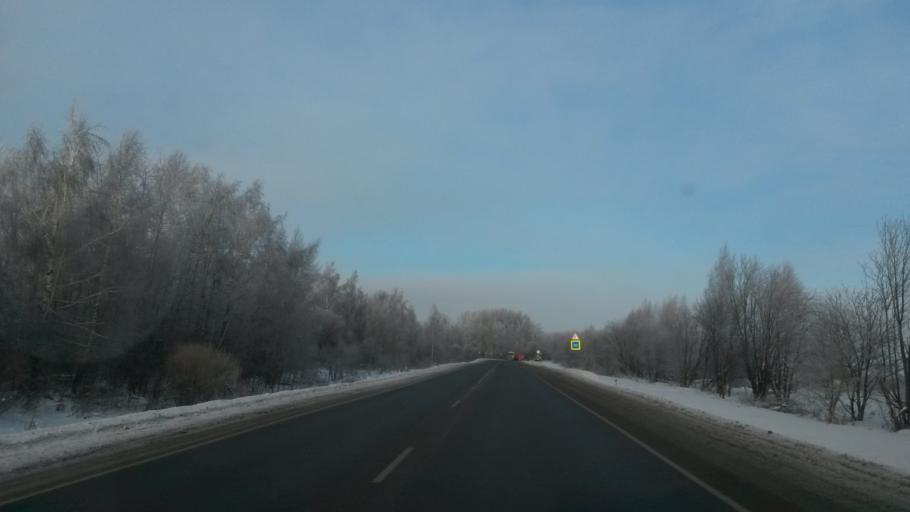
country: RU
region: Vladimir
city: Bogolyubovo
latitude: 56.2097
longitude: 40.4414
